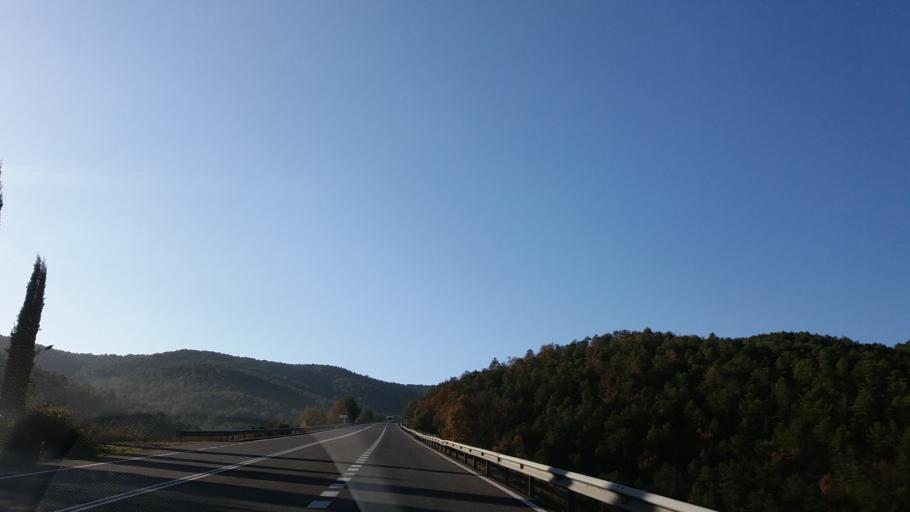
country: ES
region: Catalonia
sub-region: Provincia de Lleida
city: Tiurana
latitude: 41.9625
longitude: 1.2917
